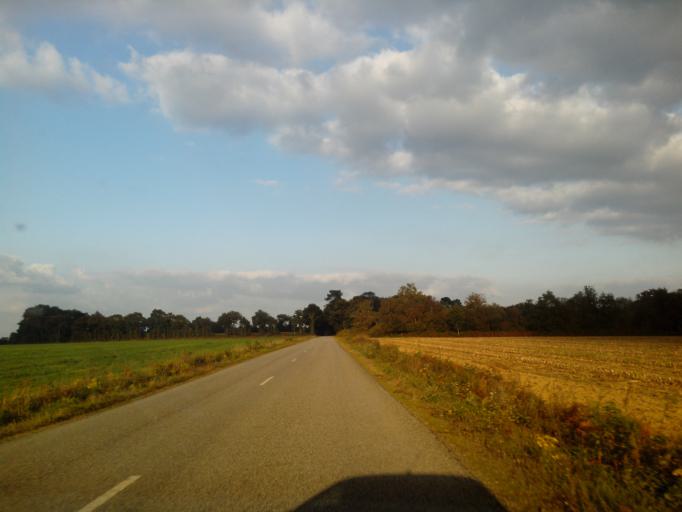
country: FR
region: Brittany
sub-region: Departement du Morbihan
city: Mauron
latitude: 48.1212
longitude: -2.2807
